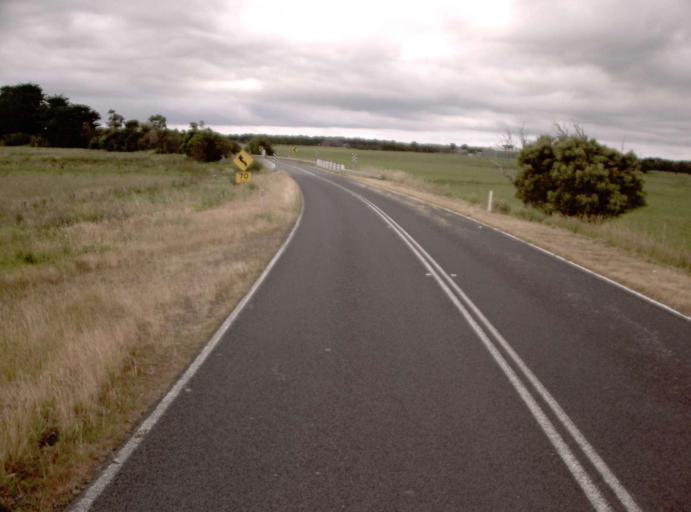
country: AU
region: Victoria
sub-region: Bass Coast
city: North Wonthaggi
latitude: -38.5732
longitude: 145.6307
